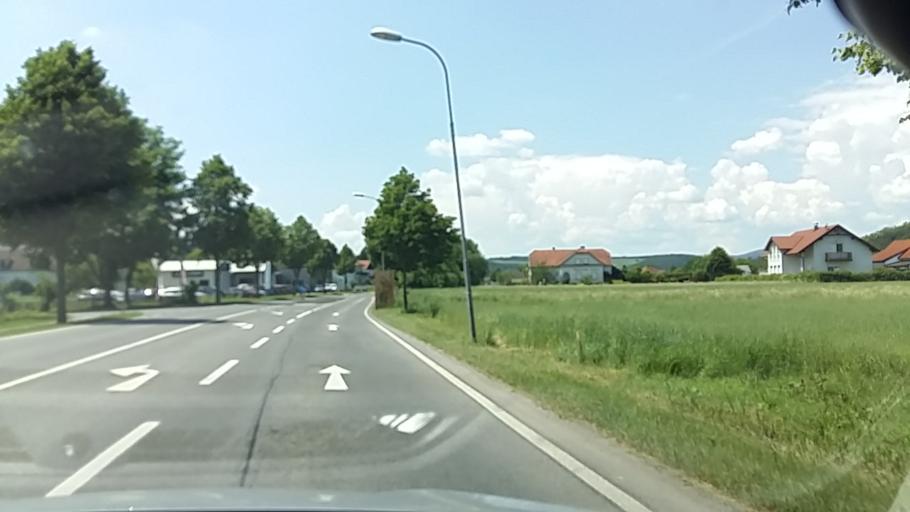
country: AT
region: Burgenland
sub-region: Politischer Bezirk Oberpullendorf
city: Piringsdorf
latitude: 47.4521
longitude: 16.4265
